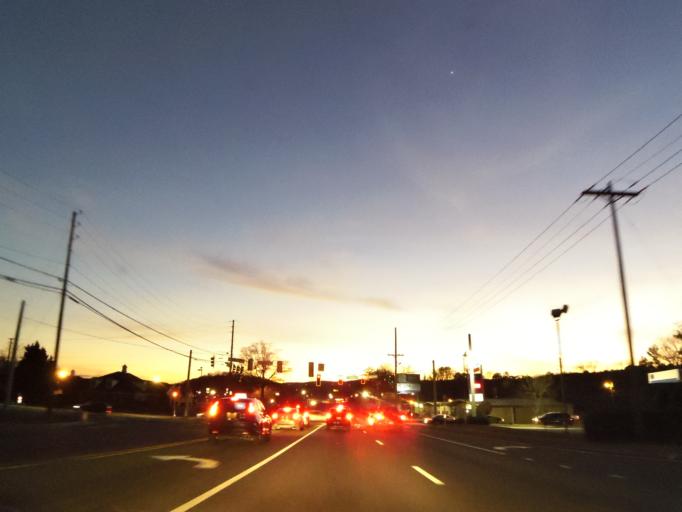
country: US
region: Georgia
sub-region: Whitfield County
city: Dalton
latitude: 34.8048
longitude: -84.9572
